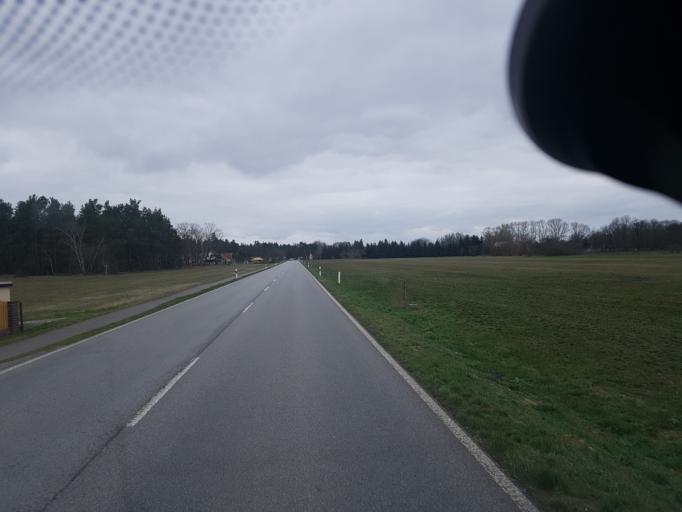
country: DE
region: Brandenburg
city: Luebben
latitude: 51.9130
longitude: 13.8657
